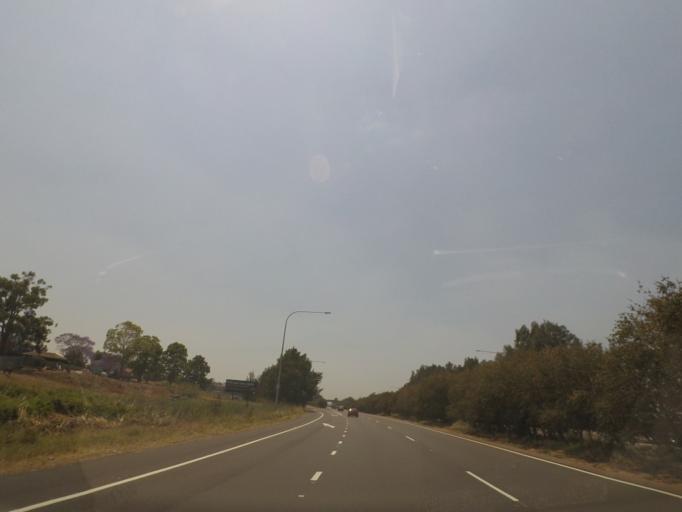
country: AU
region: New South Wales
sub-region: Newcastle
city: Beresfield
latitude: -32.8130
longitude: 151.6609
